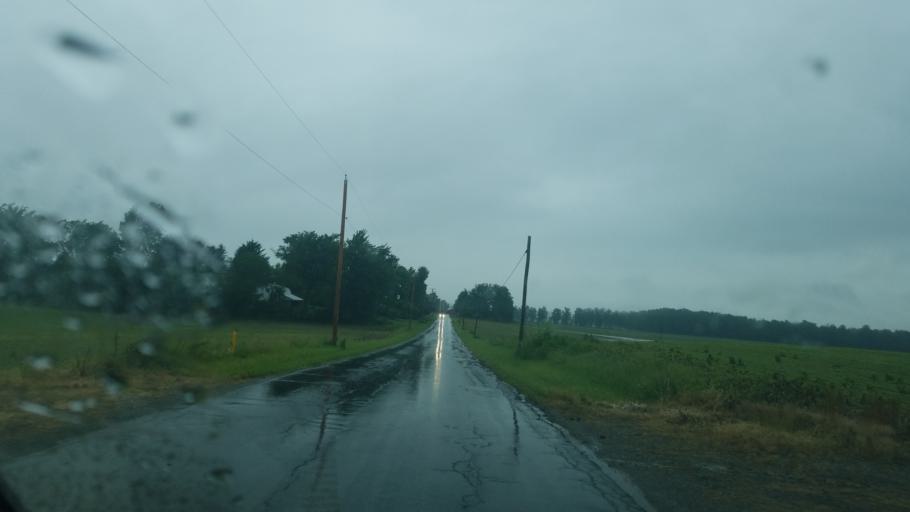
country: US
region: Ohio
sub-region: Huron County
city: Plymouth
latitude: 40.9899
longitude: -82.6050
